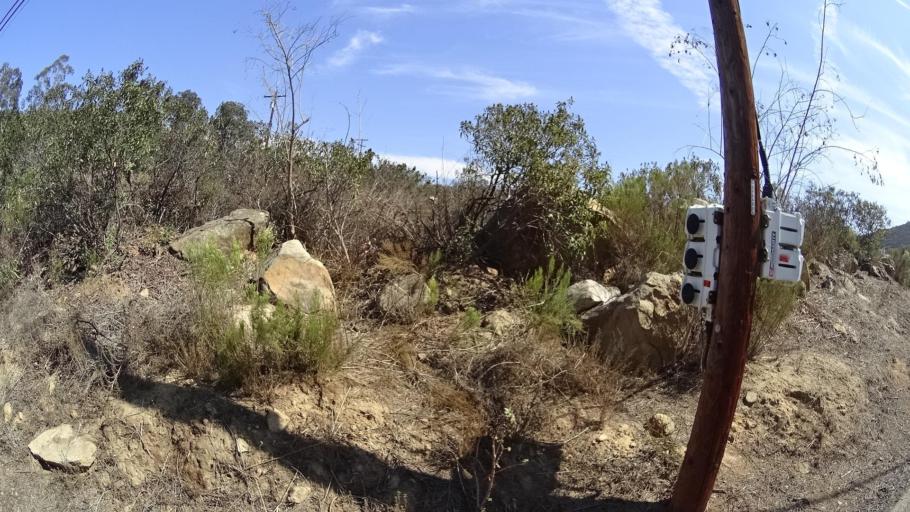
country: US
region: California
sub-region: San Diego County
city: Rancho San Diego
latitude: 32.7181
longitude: -116.9280
